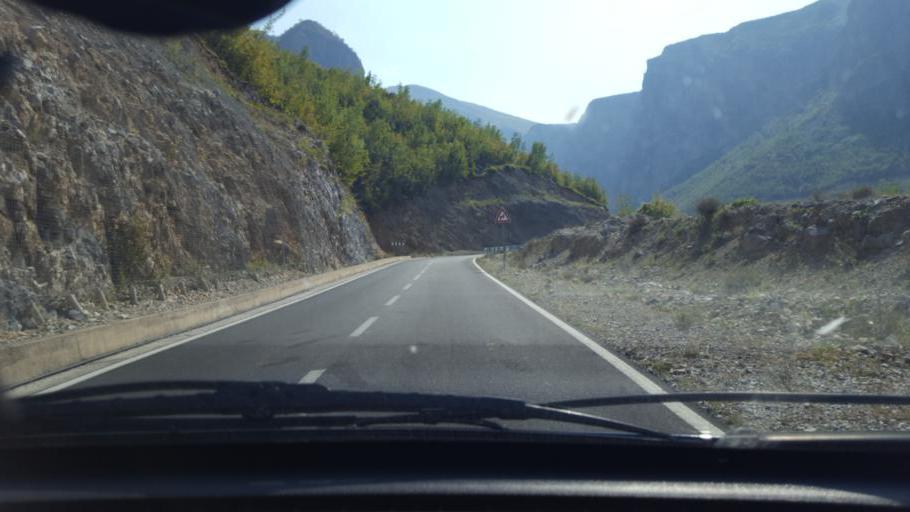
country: AL
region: Shkoder
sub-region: Rrethi i Malesia e Madhe
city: Kastrat
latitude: 42.4213
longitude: 19.5107
